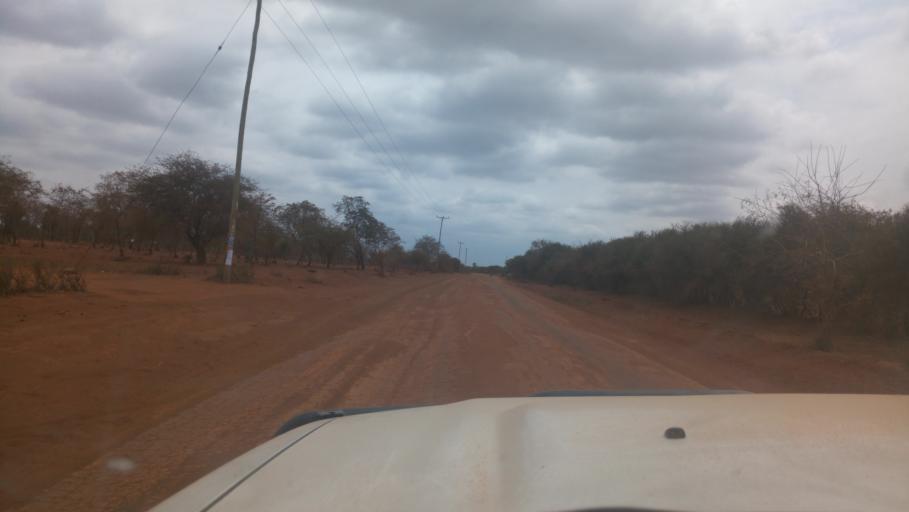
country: KE
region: Makueni
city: Wote
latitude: -1.8129
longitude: 37.9281
